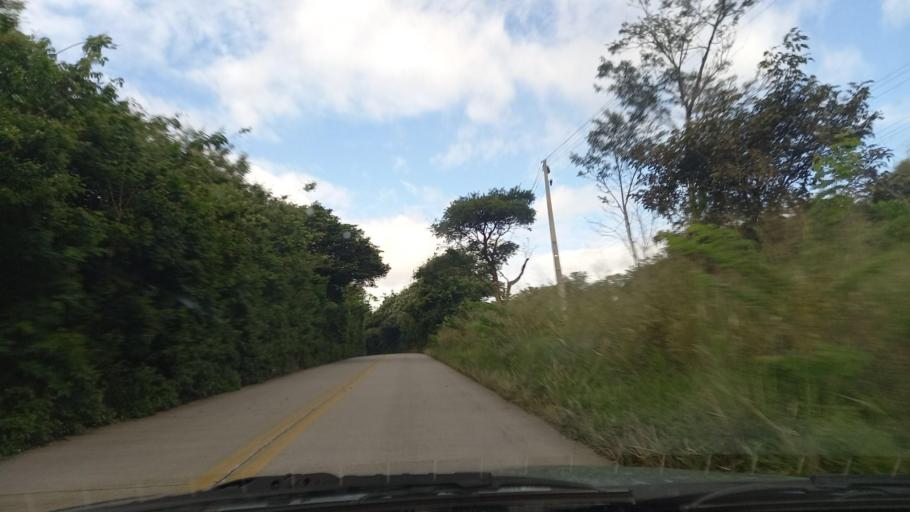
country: BR
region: Pernambuco
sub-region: Quipapa
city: Quipapa
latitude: -8.7882
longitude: -35.9663
